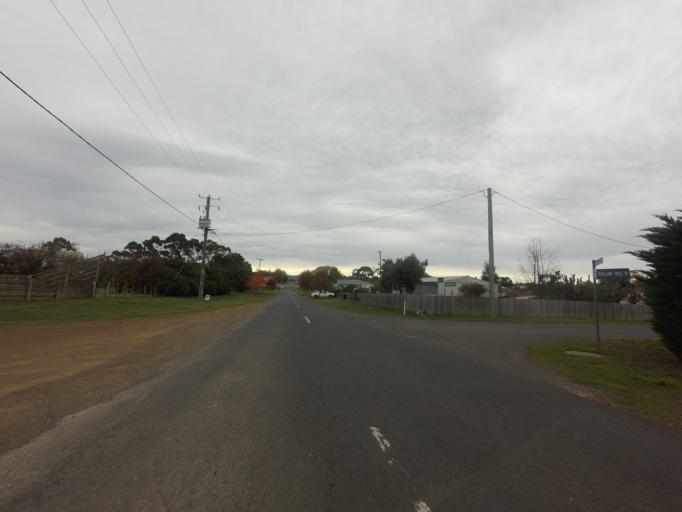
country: AU
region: Tasmania
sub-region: Derwent Valley
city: New Norfolk
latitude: -42.3865
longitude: 147.0072
